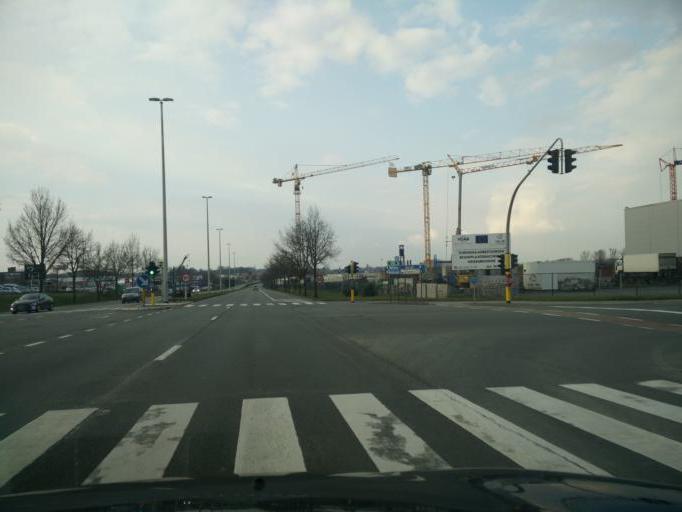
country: BE
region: Flanders
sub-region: Provincie Oost-Vlaanderen
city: Perre
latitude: 50.8744
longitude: 3.8393
